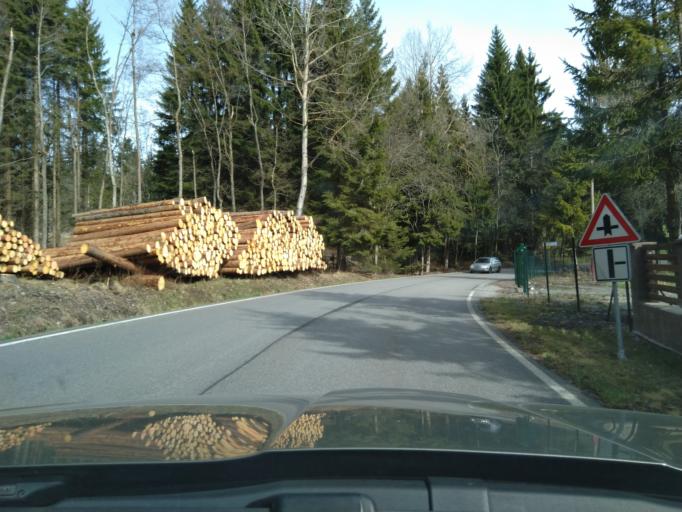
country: CZ
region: Jihocesky
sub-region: Okres Prachatice
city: Stachy
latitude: 49.0894
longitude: 13.6384
